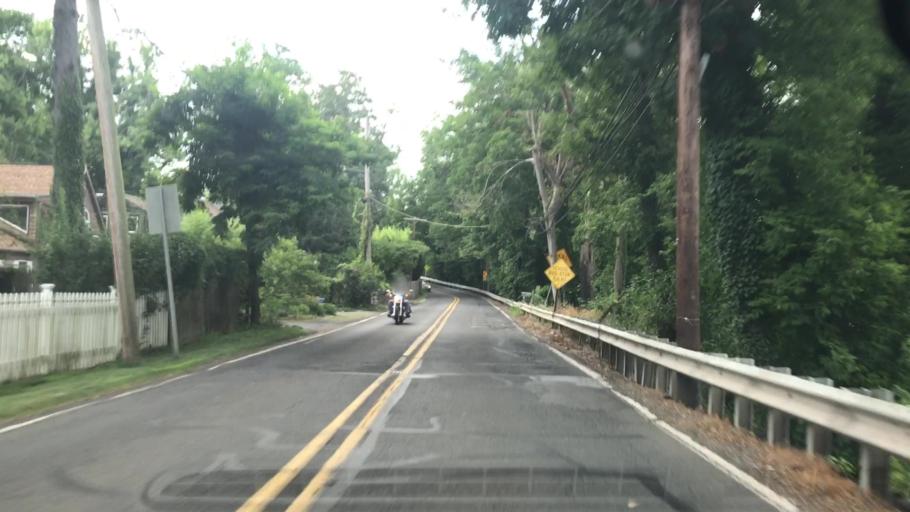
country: US
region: Pennsylvania
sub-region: Bucks County
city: New Hope
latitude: 40.3740
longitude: -74.9552
